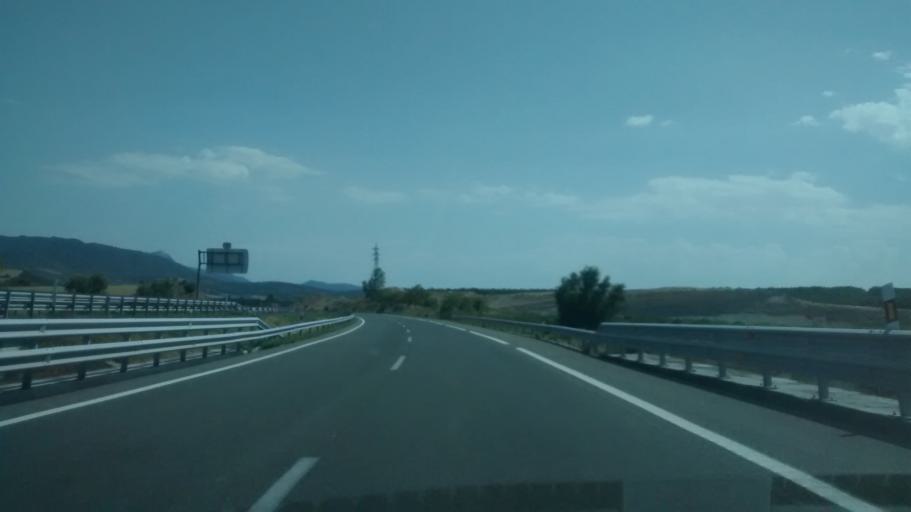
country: ES
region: Basque Country
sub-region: Provincia de Alava
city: Arminon
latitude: 42.7014
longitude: -2.8995
